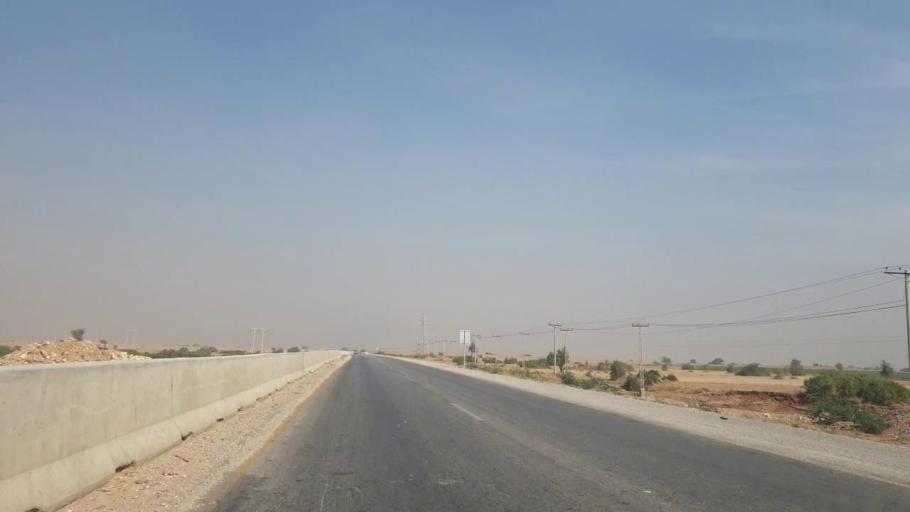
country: PK
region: Sindh
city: Jamshoro
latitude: 25.5237
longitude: 68.2762
